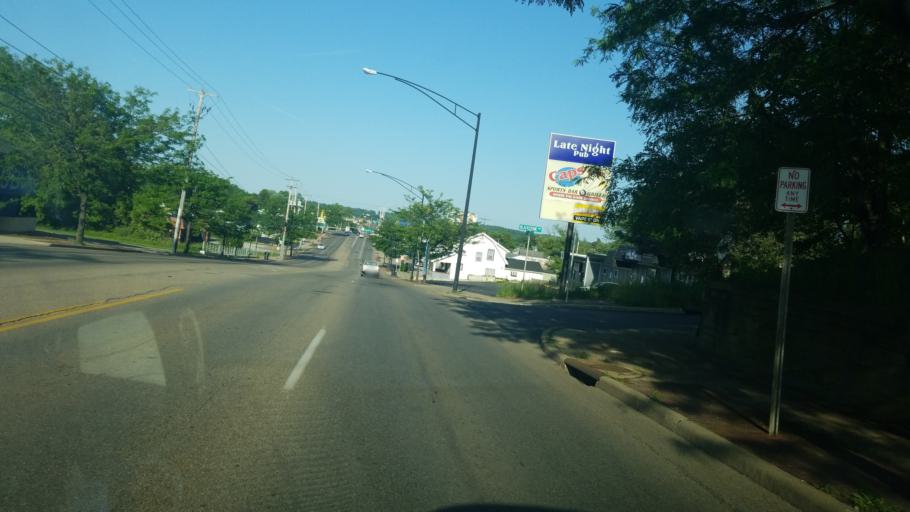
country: US
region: Ohio
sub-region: Summit County
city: Tallmadge
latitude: 41.1019
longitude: -81.4702
